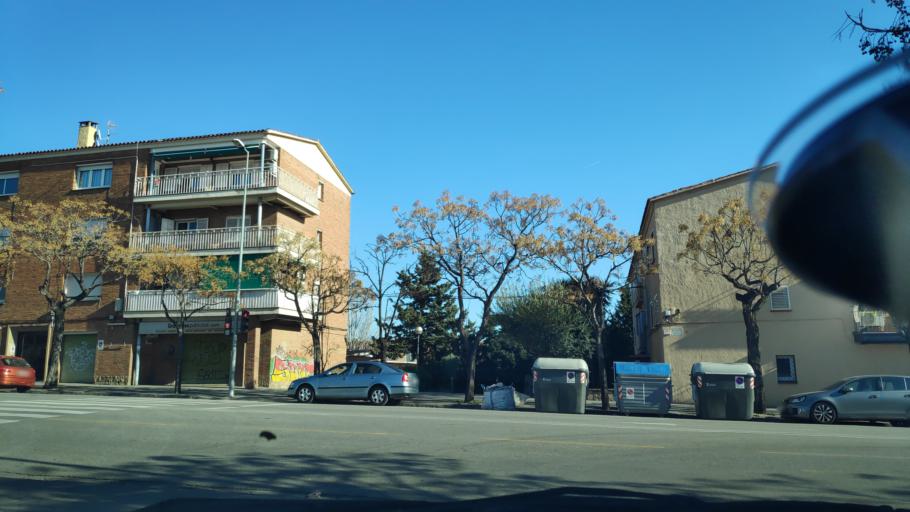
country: ES
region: Catalonia
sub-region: Provincia de Barcelona
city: Sant Quirze del Valles
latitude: 41.5422
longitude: 2.0936
